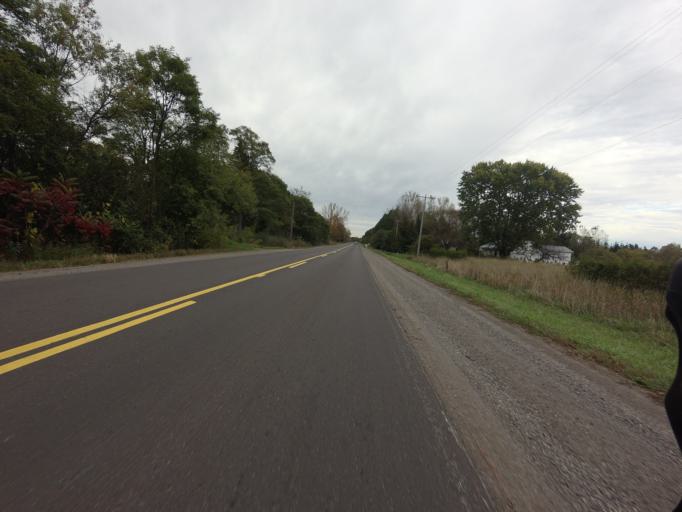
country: CA
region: Ontario
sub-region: Lanark County
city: Smiths Falls
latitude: 44.9765
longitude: -75.8159
